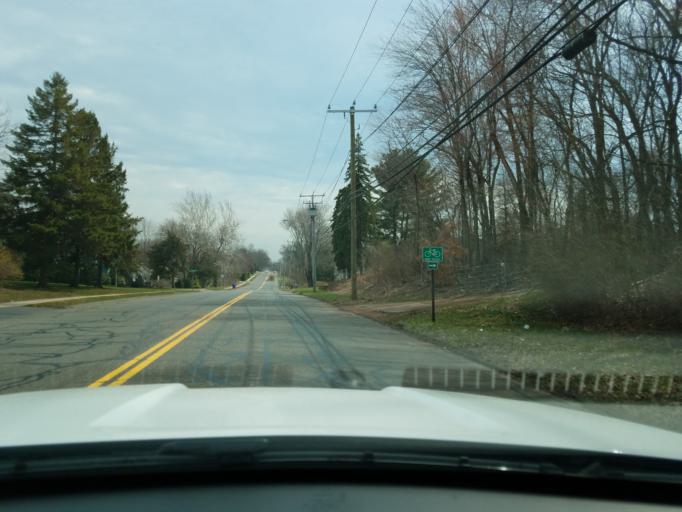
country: US
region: Connecticut
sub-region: Hartford County
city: Newington
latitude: 41.6771
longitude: -72.6898
